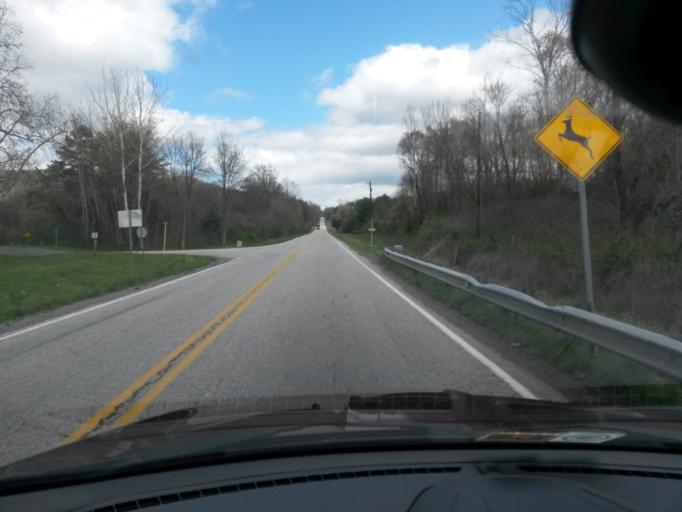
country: US
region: Virginia
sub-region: Rockbridge County
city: Glasgow
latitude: 37.6497
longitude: -79.4282
